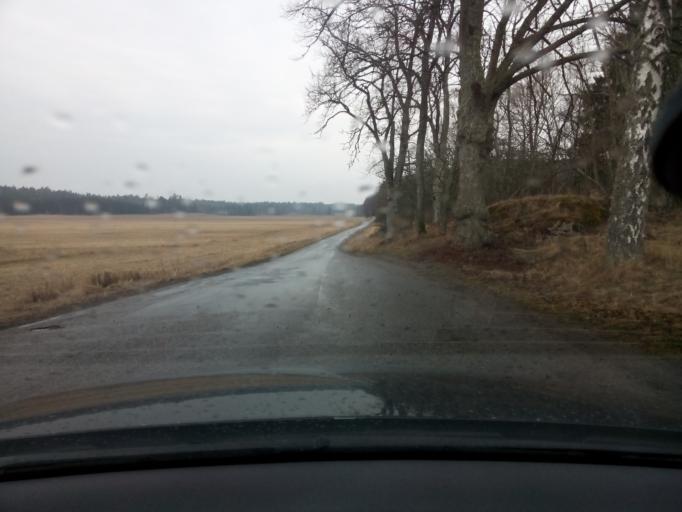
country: SE
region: Soedermanland
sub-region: Trosa Kommun
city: Trosa
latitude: 58.9033
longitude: 17.5964
